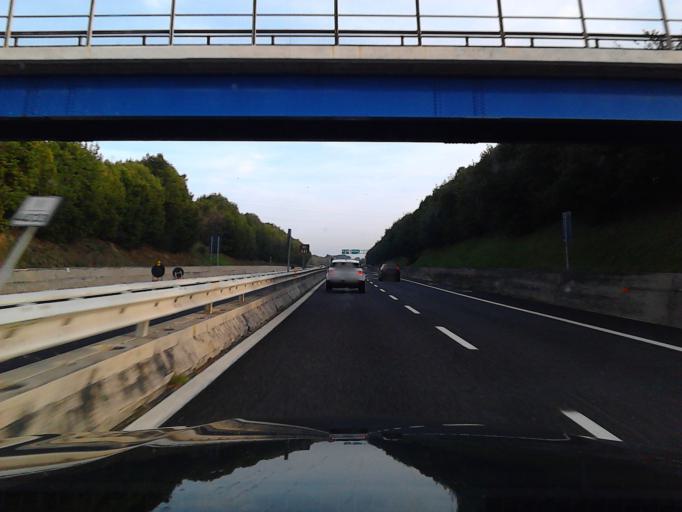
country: IT
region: Abruzzo
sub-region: Provincia di Chieti
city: Ortona
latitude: 42.3331
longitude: 14.3741
